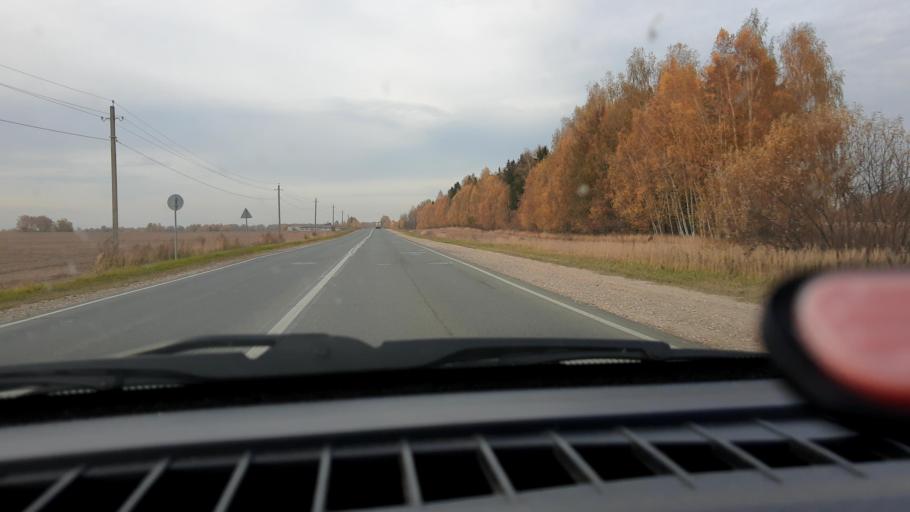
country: RU
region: Nizjnij Novgorod
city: Gorodets
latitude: 56.6181
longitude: 43.5582
